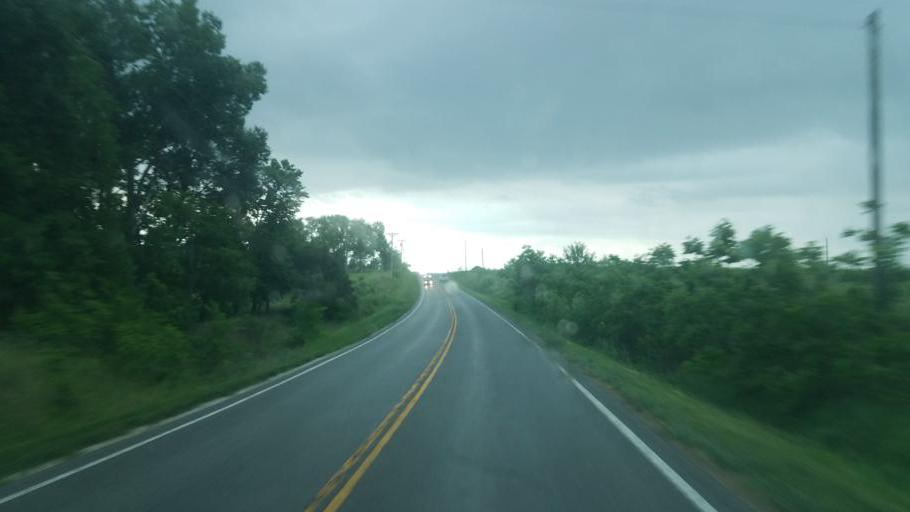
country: US
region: Missouri
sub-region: Cooper County
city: Boonville
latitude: 38.9111
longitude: -92.6817
